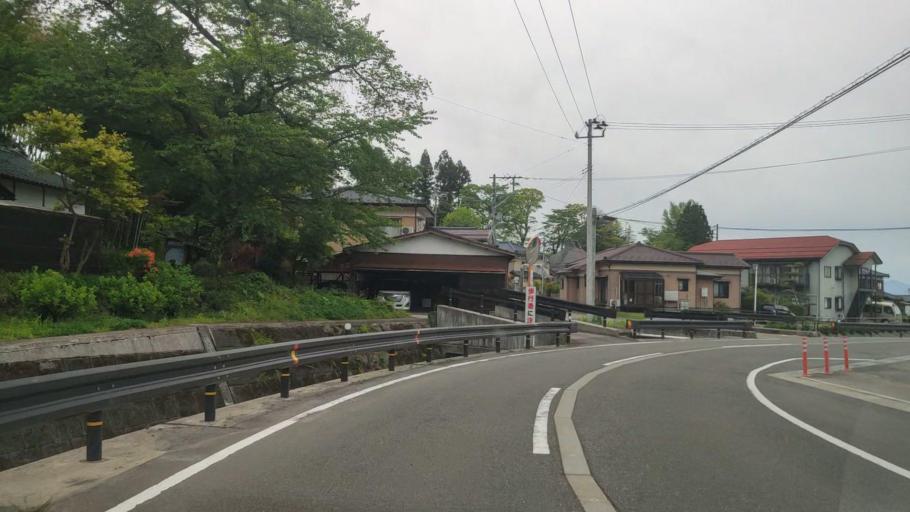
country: JP
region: Niigata
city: Kamo
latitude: 37.7115
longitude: 139.0781
